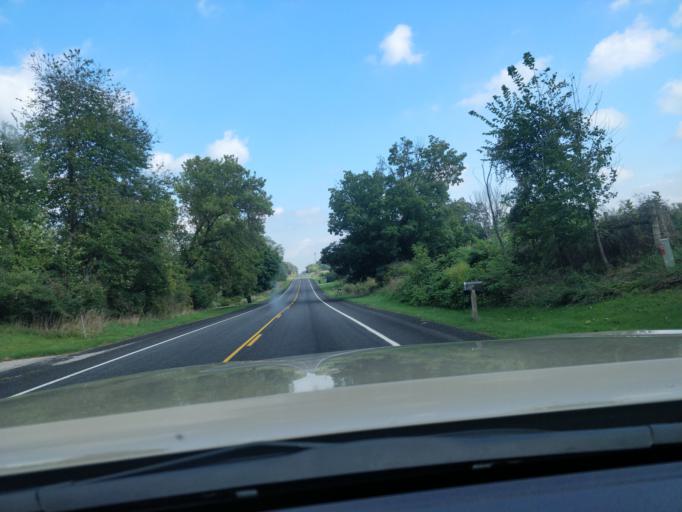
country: US
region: Michigan
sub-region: Ionia County
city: Saranac
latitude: 42.8862
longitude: -85.1841
